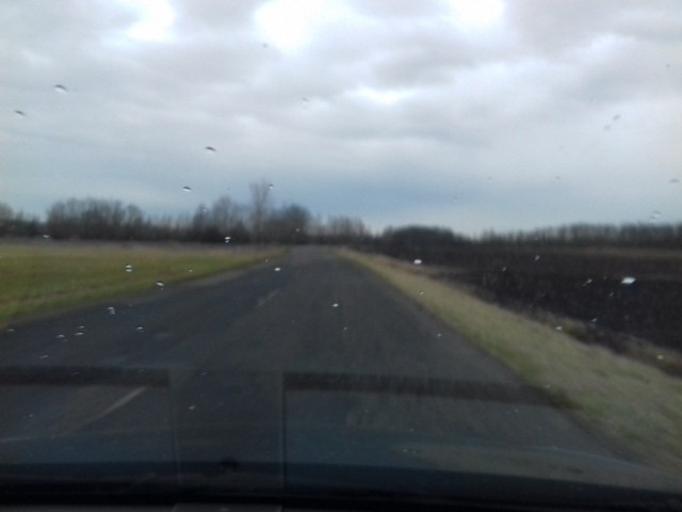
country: HU
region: Szabolcs-Szatmar-Bereg
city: Nyirbogdany
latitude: 48.0499
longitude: 21.8624
